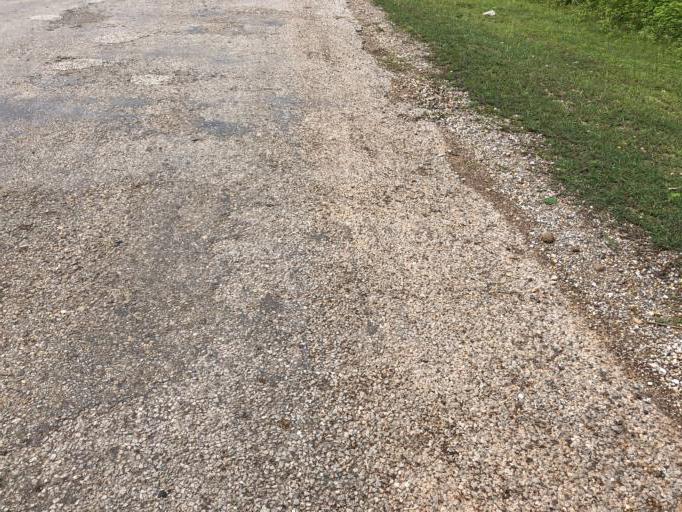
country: TH
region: Mukdahan
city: Wan Yai
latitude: 16.7702
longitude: 104.8557
